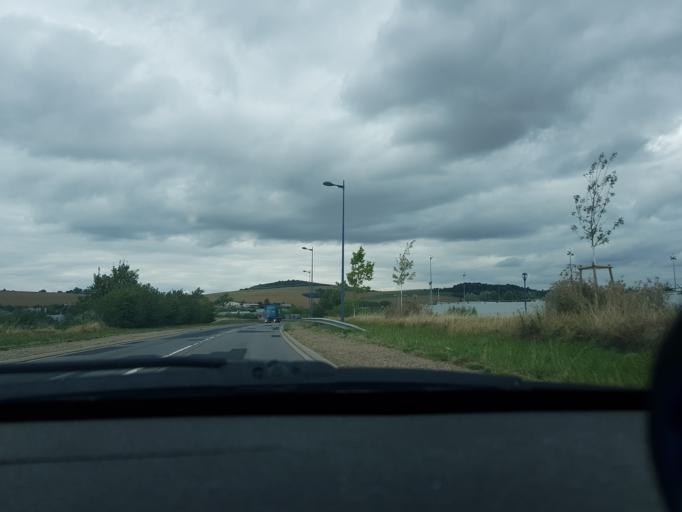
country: FR
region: Lorraine
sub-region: Departement de Meurthe-et-Moselle
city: Saulxures-les-Nancy
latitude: 48.7043
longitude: 6.2421
